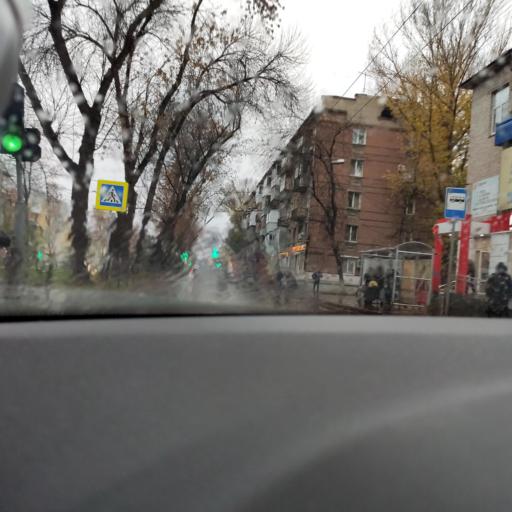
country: RU
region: Samara
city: Petra-Dubrava
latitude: 53.2370
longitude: 50.2782
